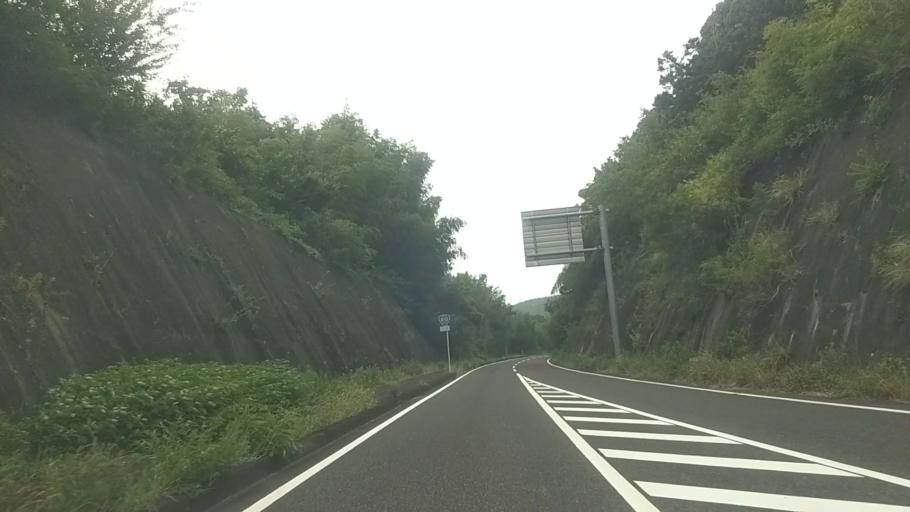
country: JP
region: Chiba
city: Kawaguchi
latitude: 35.2210
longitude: 140.0221
